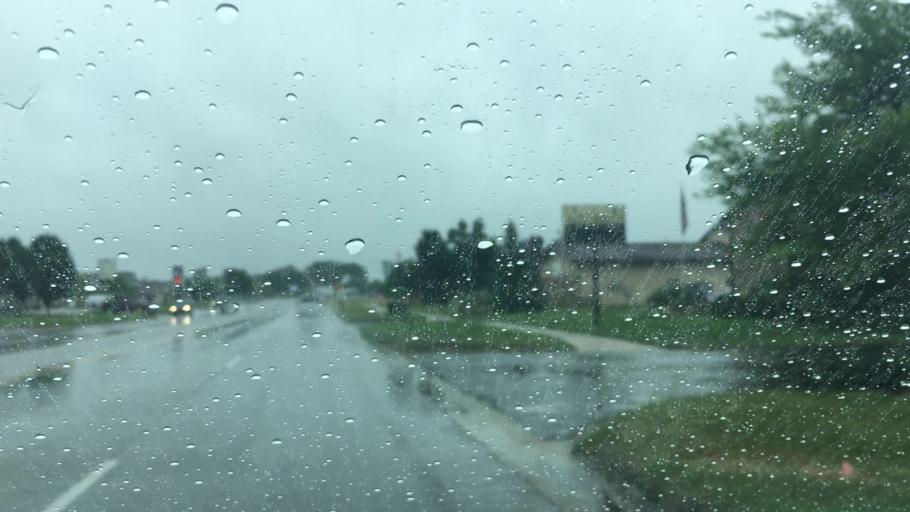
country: US
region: Michigan
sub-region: Ottawa County
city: Hudsonville
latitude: 42.8876
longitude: -85.8414
